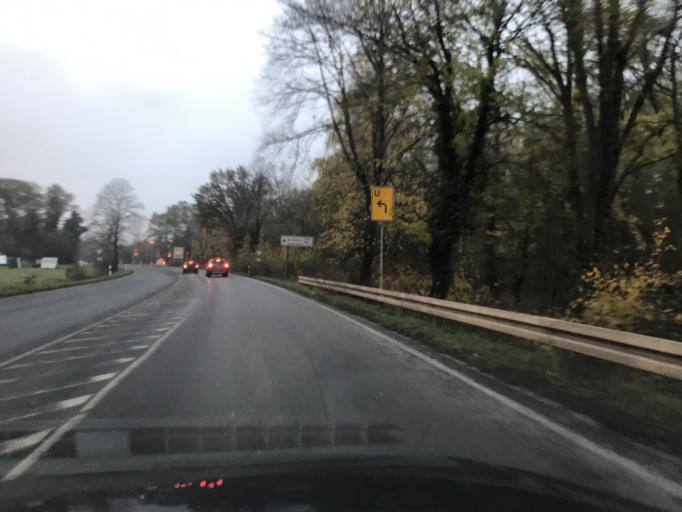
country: DE
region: North Rhine-Westphalia
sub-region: Regierungsbezirk Arnsberg
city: Welver
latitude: 51.6935
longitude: 7.9523
